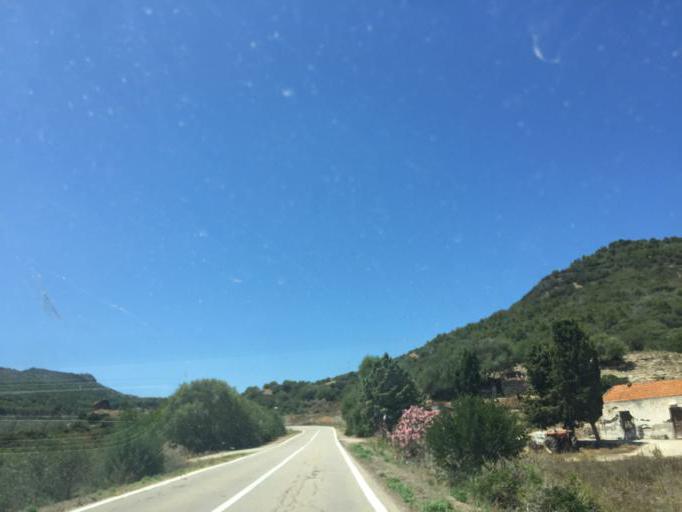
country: IT
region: Sardinia
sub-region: Provincia di Sassari
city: Castelsardo
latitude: 40.8961
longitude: 8.7589
